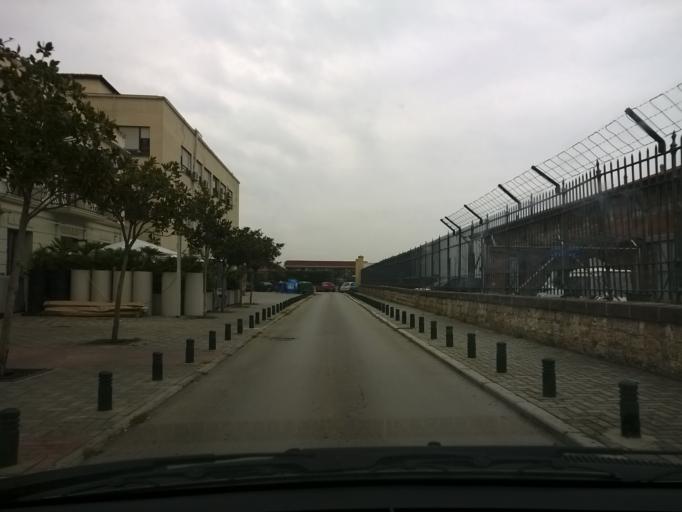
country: GR
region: Central Macedonia
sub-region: Nomos Thessalonikis
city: Thessaloniki
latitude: 40.6340
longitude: 22.9354
